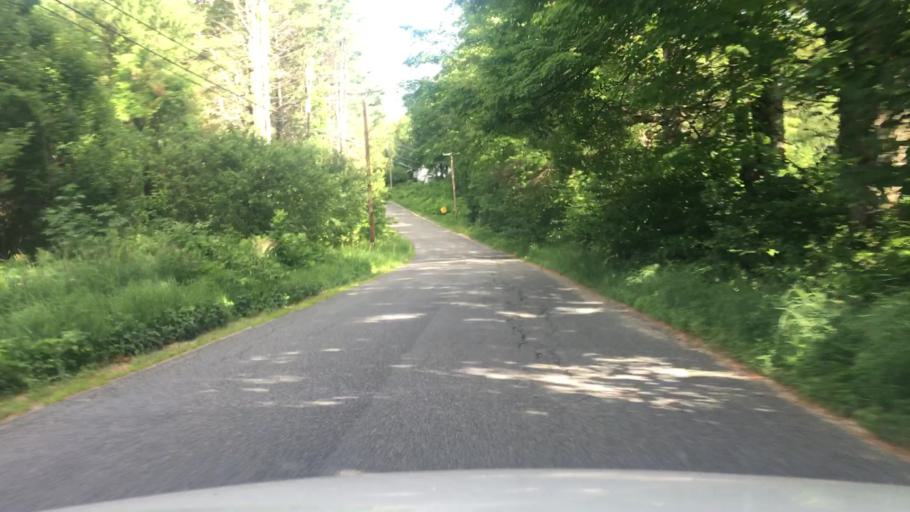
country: US
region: Maine
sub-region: Franklin County
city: Wilton
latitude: 44.6013
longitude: -70.2236
